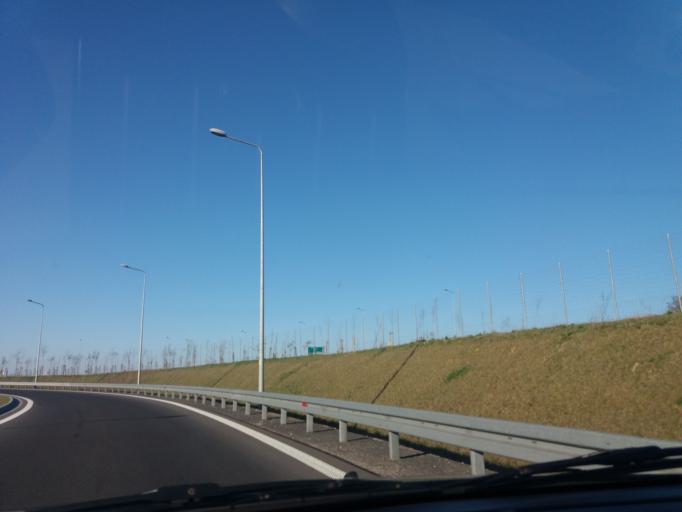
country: PL
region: Warmian-Masurian Voivodeship
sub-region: Powiat nidzicki
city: Nidzica
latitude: 53.3328
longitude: 20.4391
